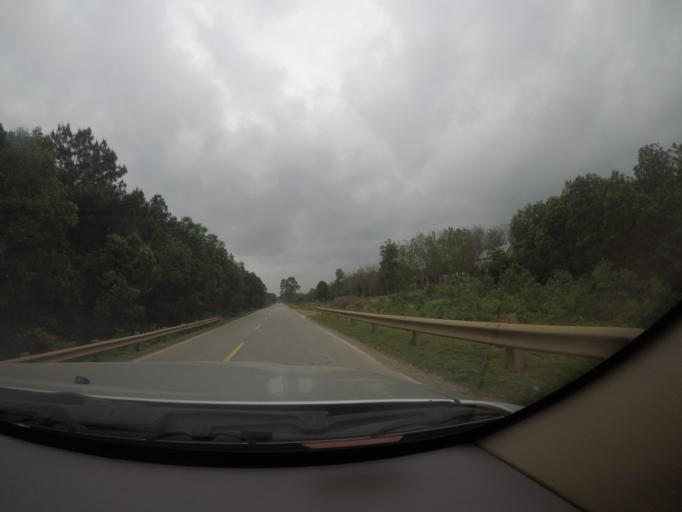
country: VN
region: Quang Binh
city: Kien Giang
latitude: 17.1681
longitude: 106.7401
